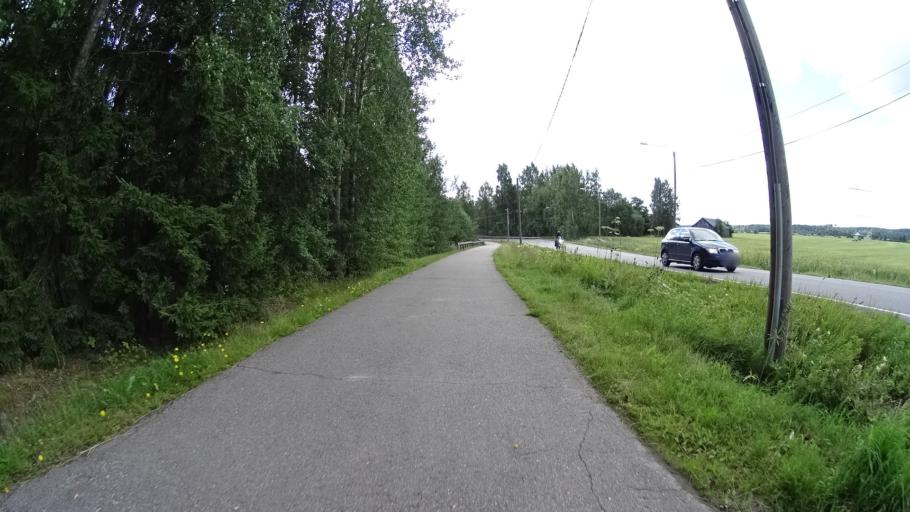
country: FI
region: Uusimaa
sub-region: Helsinki
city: Tuusula
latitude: 60.3401
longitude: 24.9207
